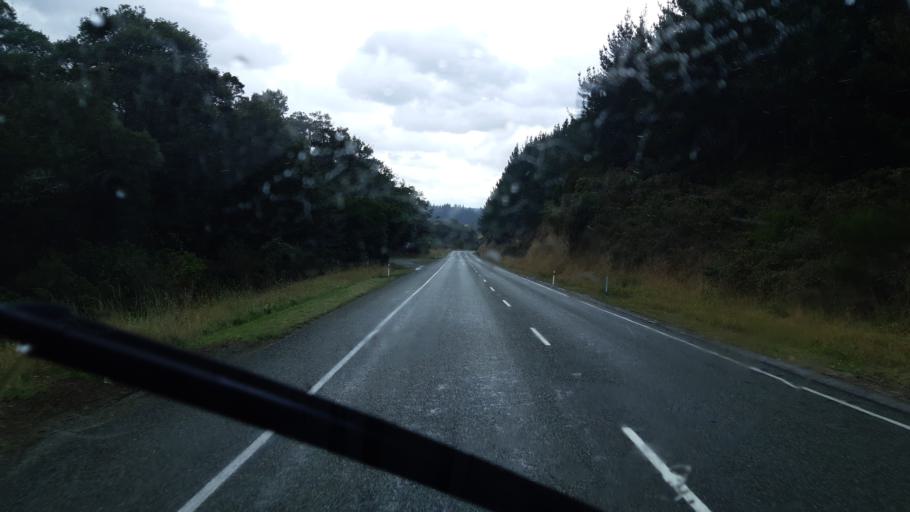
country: NZ
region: Tasman
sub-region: Tasman District
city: Wakefield
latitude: -41.4781
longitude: 172.9295
